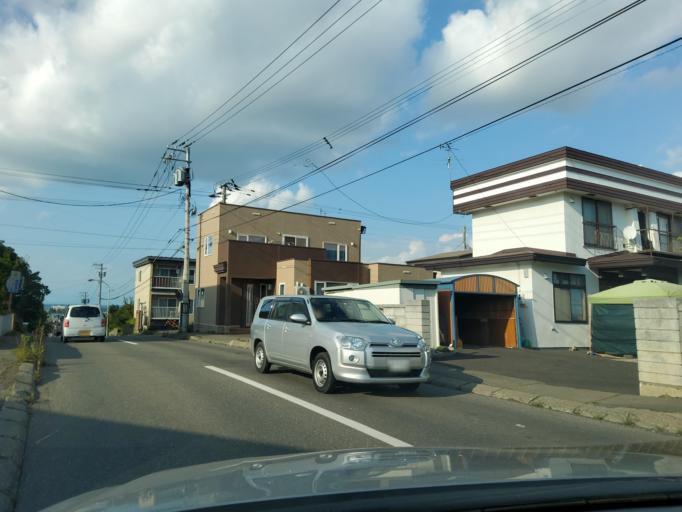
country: JP
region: Hokkaido
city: Obihiro
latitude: 42.9008
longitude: 143.1740
